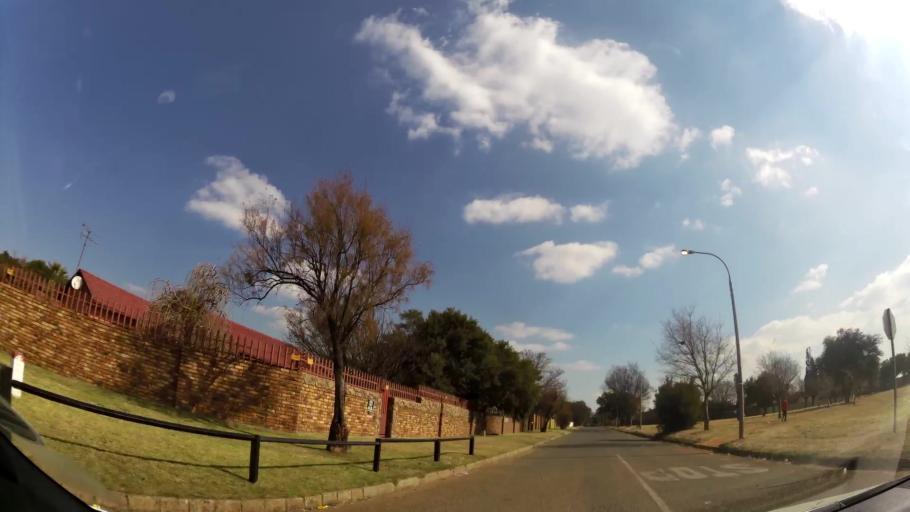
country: ZA
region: Gauteng
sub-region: Ekurhuleni Metropolitan Municipality
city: Boksburg
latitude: -26.1954
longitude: 28.2117
